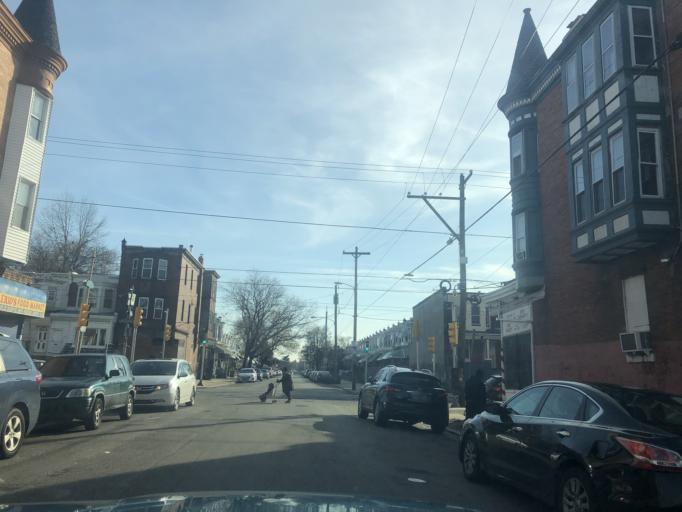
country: US
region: Pennsylvania
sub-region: Delaware County
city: Millbourne
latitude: 39.9772
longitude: -75.2319
